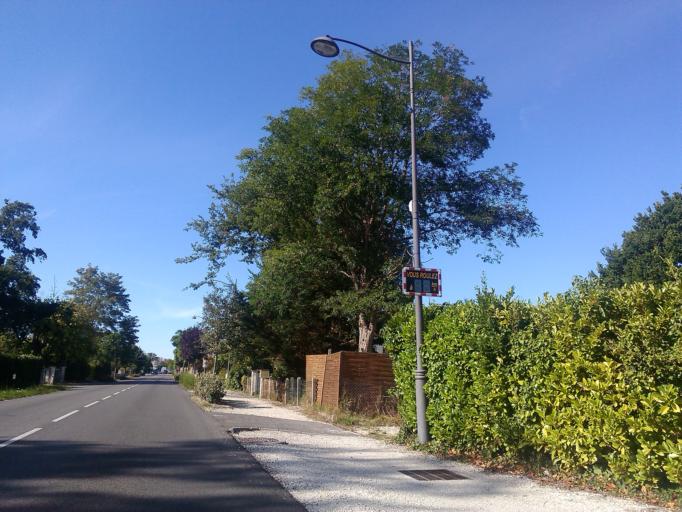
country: FR
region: Aquitaine
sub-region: Departement de la Gironde
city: Hourtin
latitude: 45.1811
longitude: -1.0559
